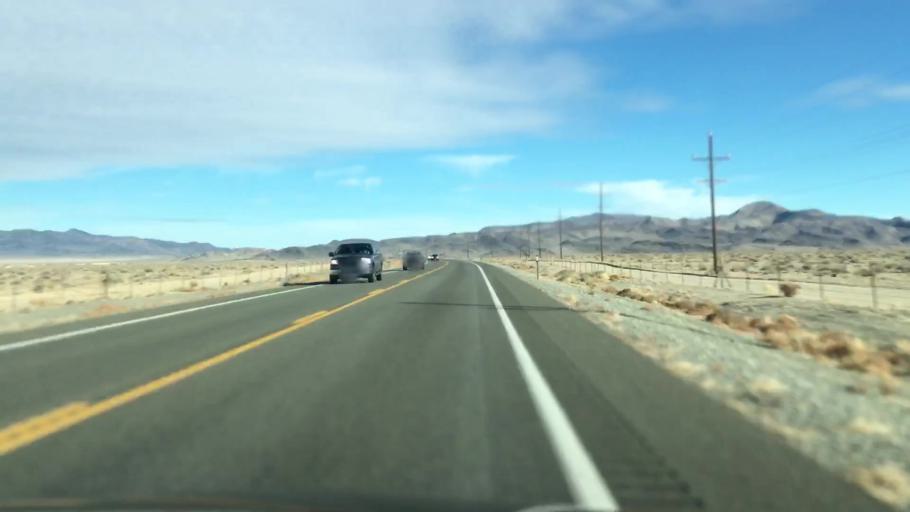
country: US
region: Nevada
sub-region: Mineral County
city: Hawthorne
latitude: 38.5246
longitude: -118.5818
